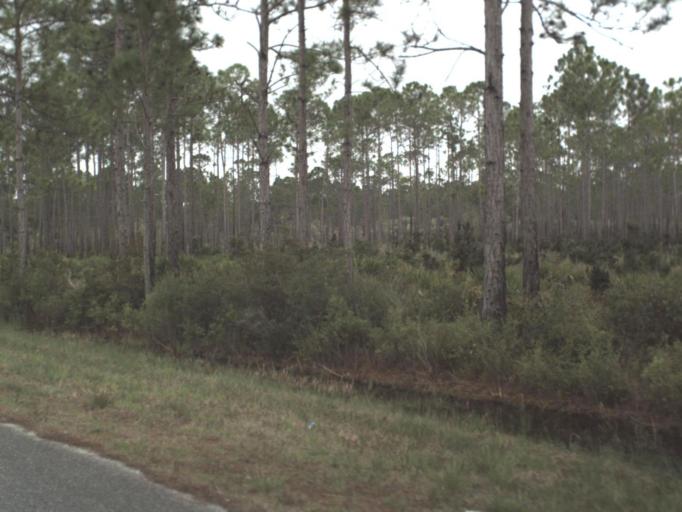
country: US
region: Florida
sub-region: Franklin County
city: Eastpoint
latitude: 29.8131
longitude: -84.8439
